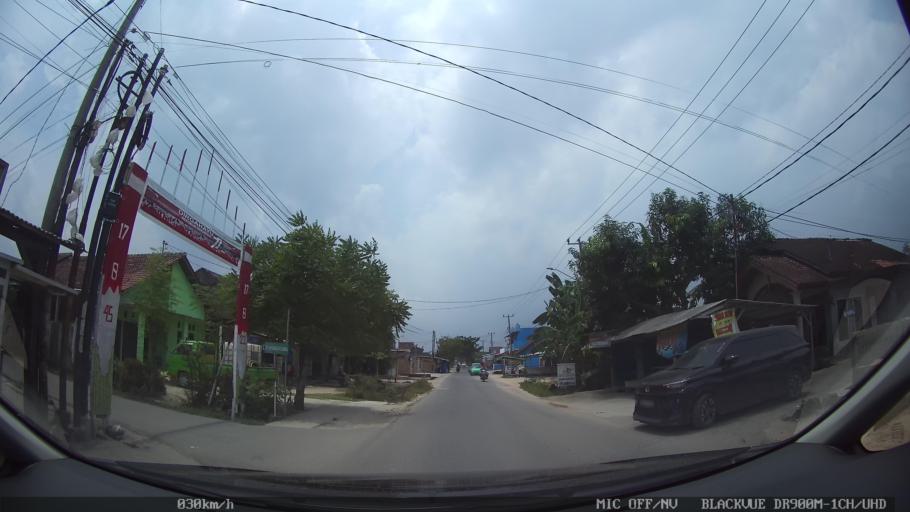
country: ID
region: Lampung
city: Kedaton
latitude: -5.3943
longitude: 105.3089
